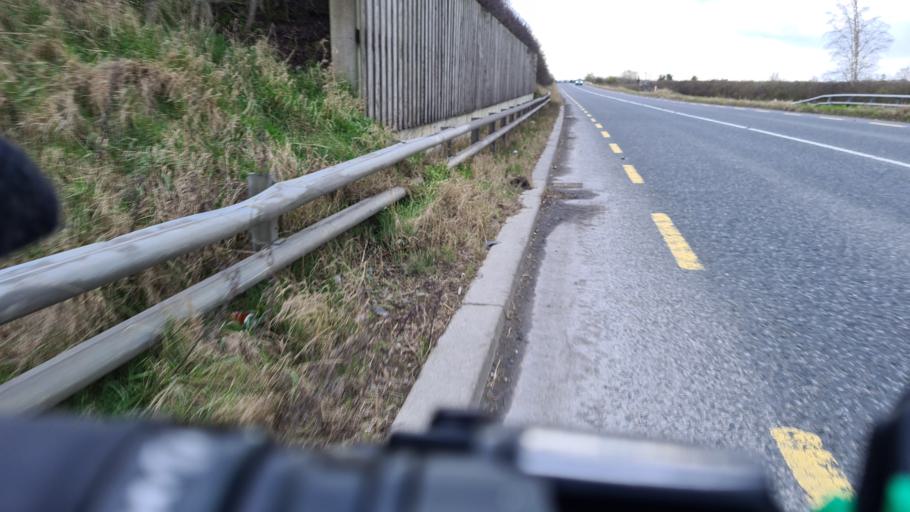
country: IE
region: Leinster
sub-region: Kildare
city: Maynooth
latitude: 53.3448
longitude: -6.6020
